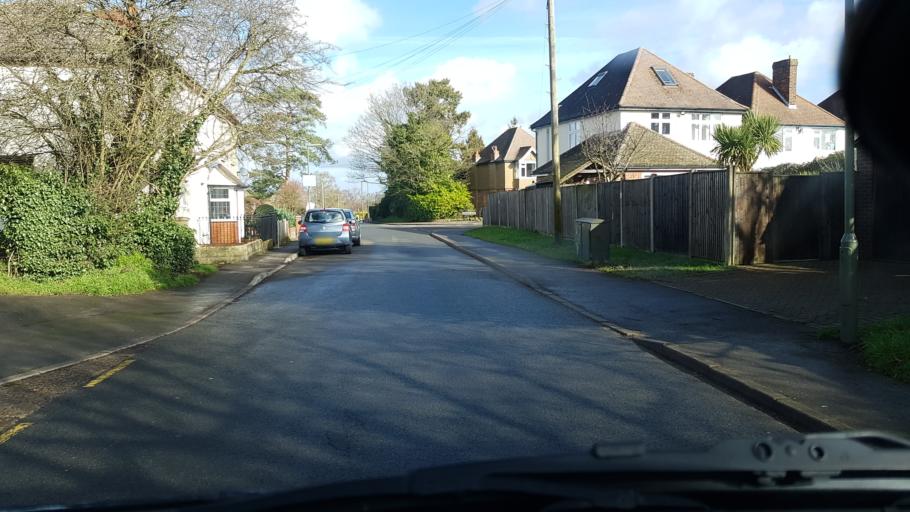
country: GB
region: England
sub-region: Surrey
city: Guildford
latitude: 51.2562
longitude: -0.6004
